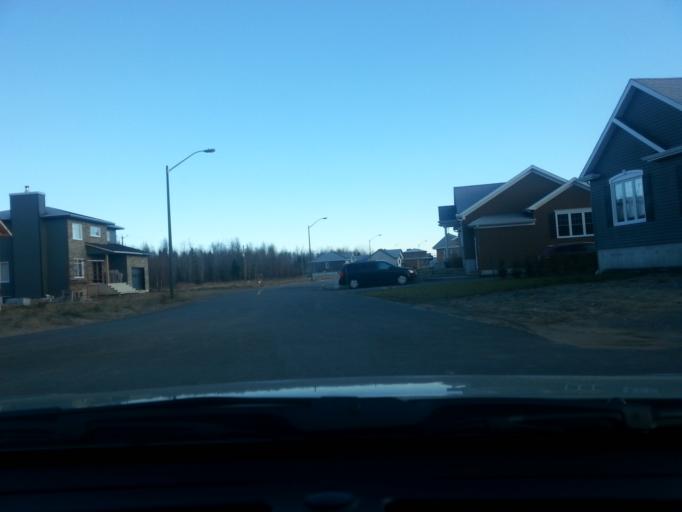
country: CA
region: Quebec
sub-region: Capitale-Nationale
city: Saint-Marc-des-Carrieres
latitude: 46.6830
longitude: -72.0721
